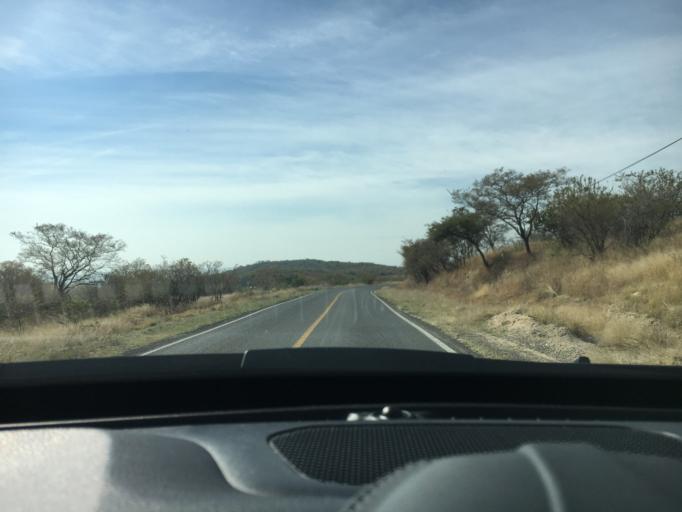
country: MX
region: Guanajuato
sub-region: Silao de la Victoria
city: San Francisco (Banos de Agua Caliente)
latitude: 21.0647
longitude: -101.5008
